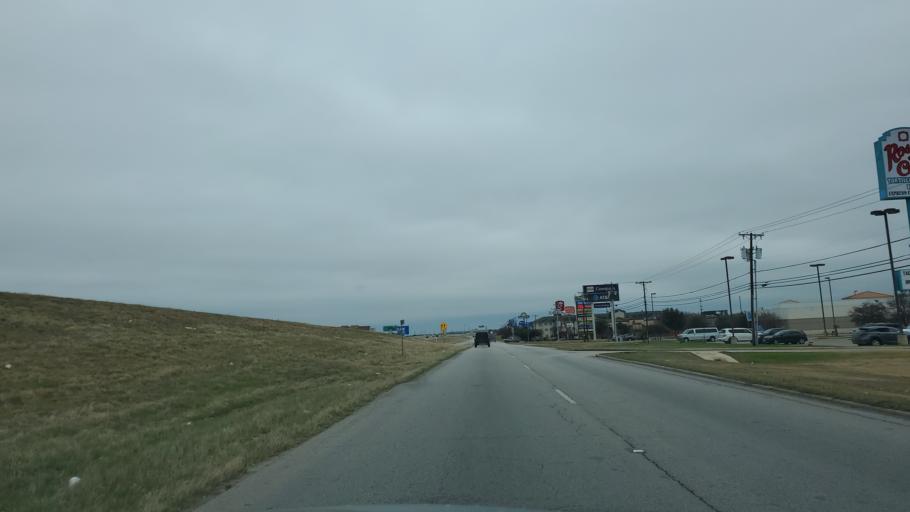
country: US
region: Texas
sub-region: Bell County
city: Killeen
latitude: 31.0938
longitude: -97.7312
